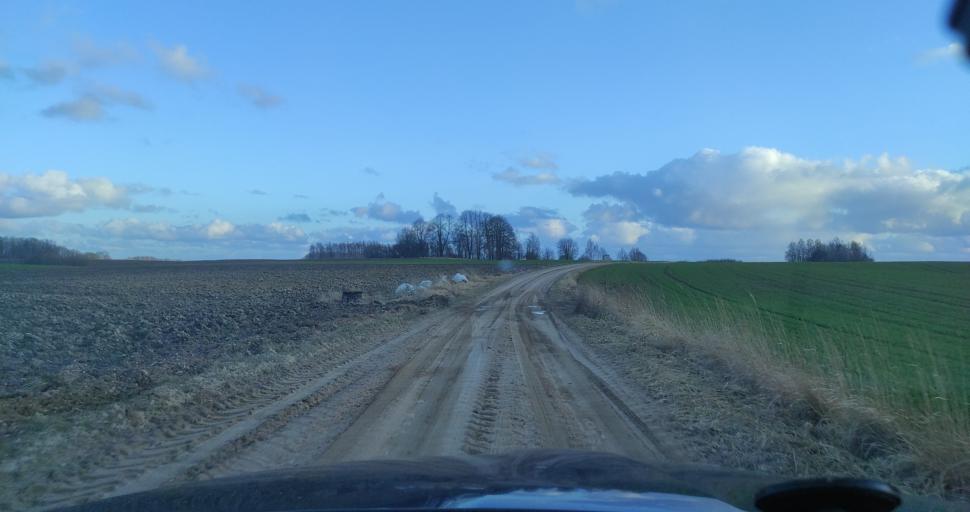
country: LV
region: Aizpute
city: Aizpute
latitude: 56.8613
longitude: 21.7606
